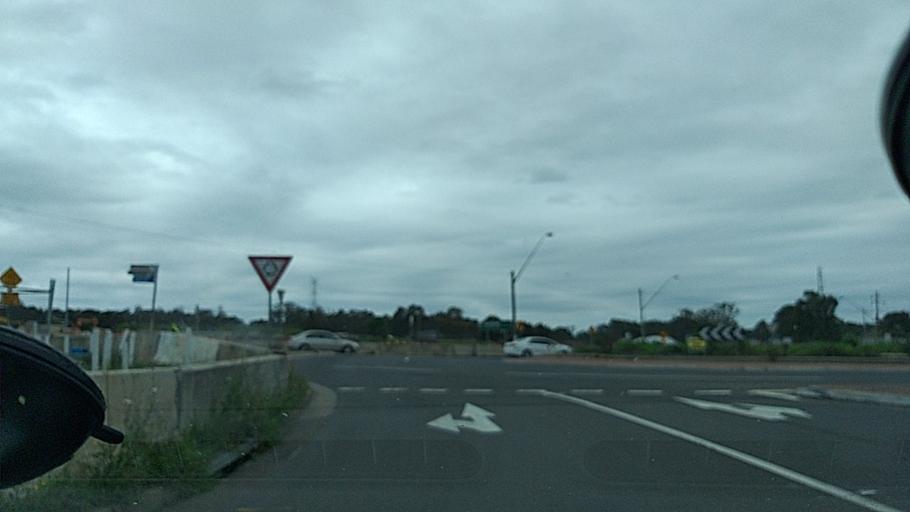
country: AU
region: New South Wales
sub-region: Penrith Municipality
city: Glenmore Park
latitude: -33.7933
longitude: 150.6992
